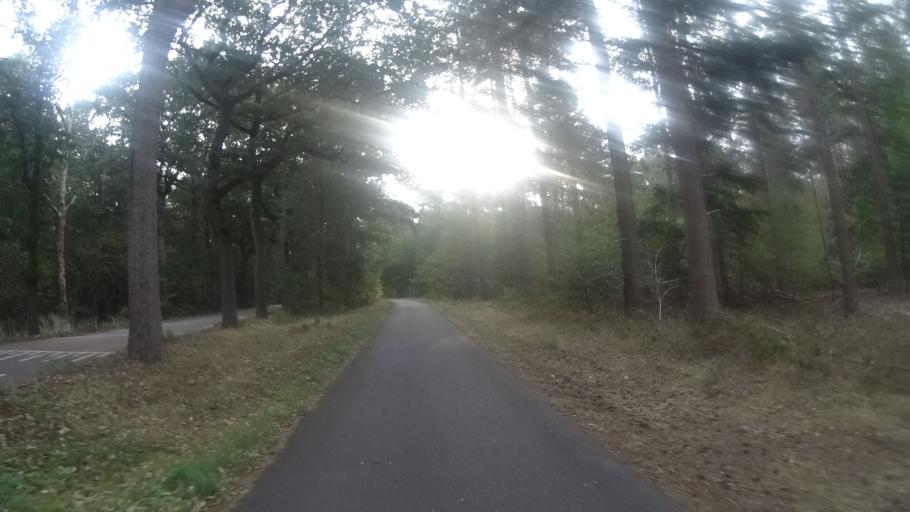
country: NL
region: Limburg
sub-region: Gemeente Venlo
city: Arcen
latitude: 51.4746
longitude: 6.2042
